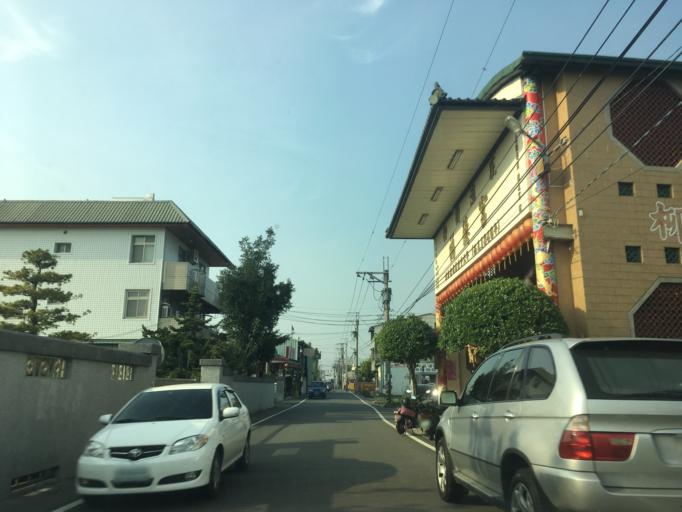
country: TW
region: Taiwan
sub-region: Taichung City
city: Taichung
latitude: 24.0672
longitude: 120.6800
